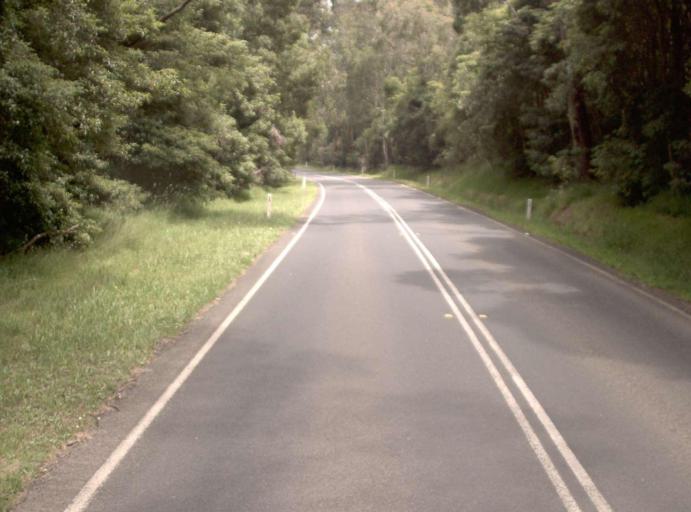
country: AU
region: Victoria
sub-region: Latrobe
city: Traralgon
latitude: -38.4326
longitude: 146.7359
